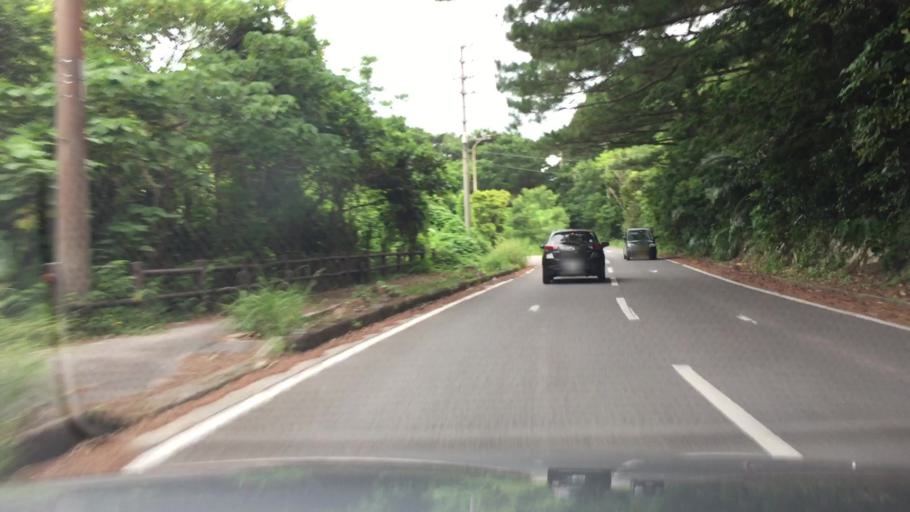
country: JP
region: Okinawa
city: Ishigaki
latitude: 24.4538
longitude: 124.1374
